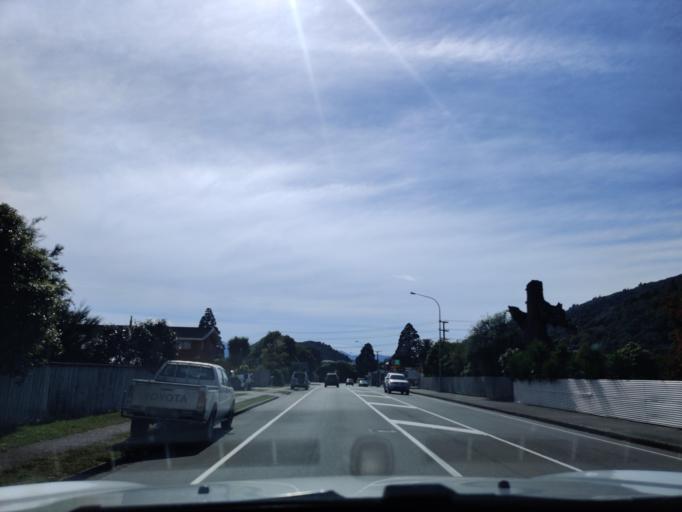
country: NZ
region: Marlborough
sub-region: Marlborough District
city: Picton
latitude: -41.2979
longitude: 174.0001
